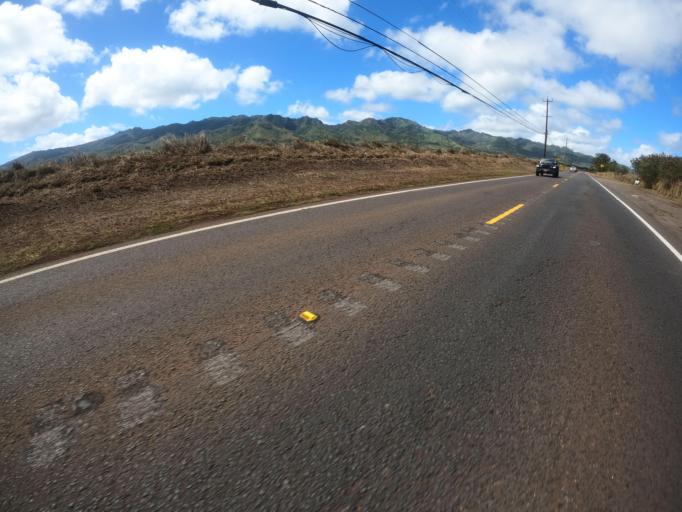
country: US
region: Hawaii
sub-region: Honolulu County
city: Village Park
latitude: 21.4243
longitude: -158.0531
